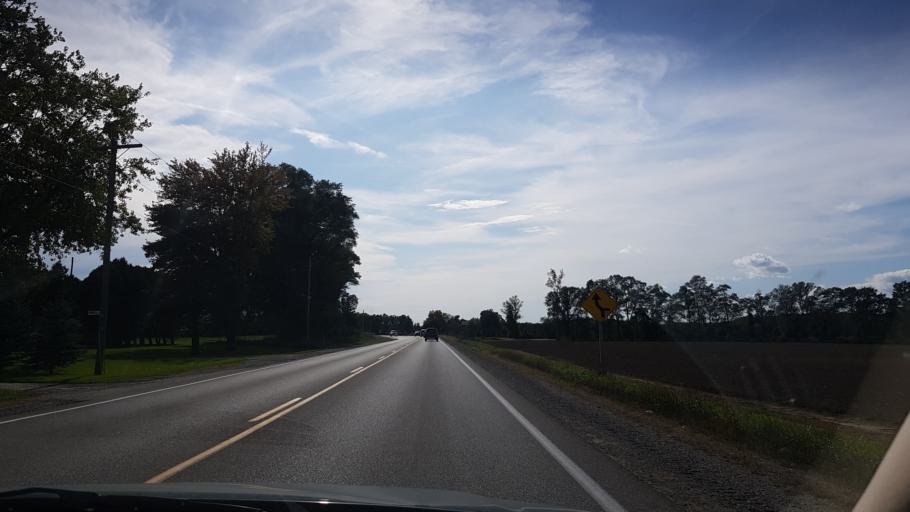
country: CA
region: Ontario
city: Delaware
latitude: 42.9310
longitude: -81.4503
